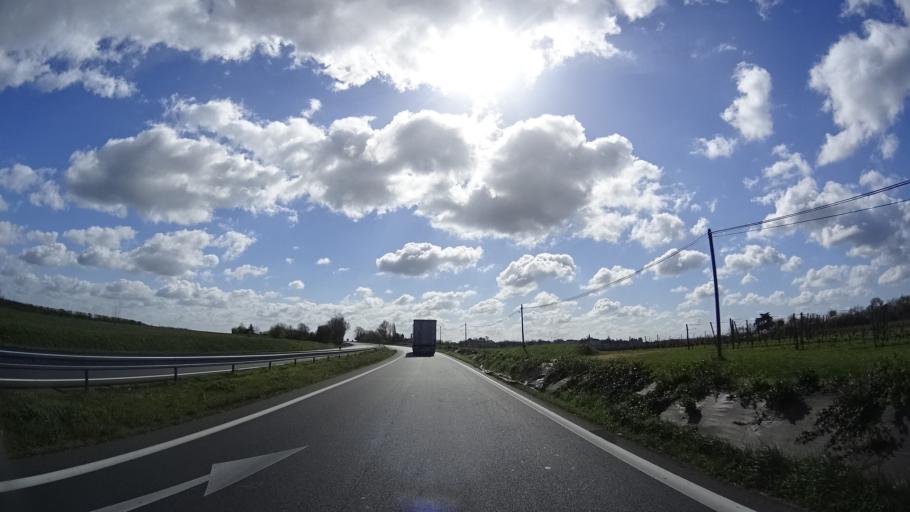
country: FR
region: Pays de la Loire
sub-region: Departement de Maine-et-Loire
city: Brissac-Quince
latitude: 47.3669
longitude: -0.4567
